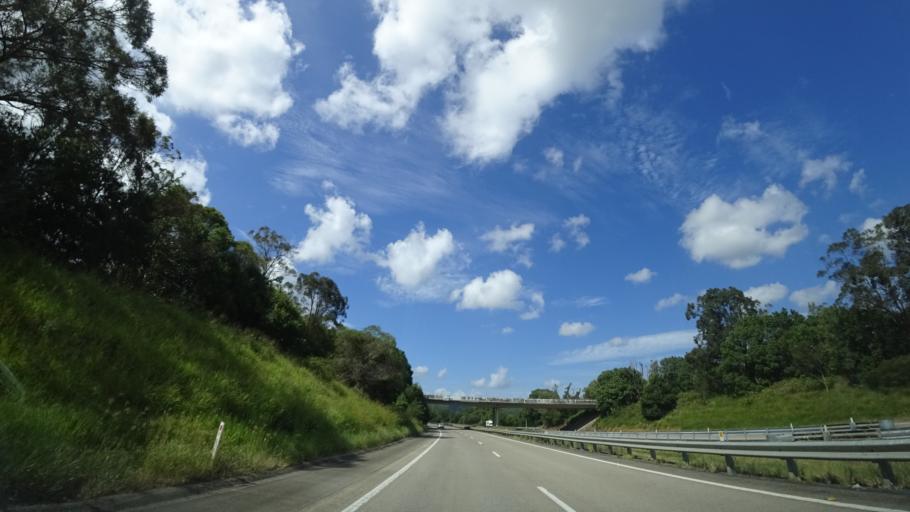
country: AU
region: Queensland
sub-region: Sunshine Coast
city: Yandina
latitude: -26.5657
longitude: 152.9657
